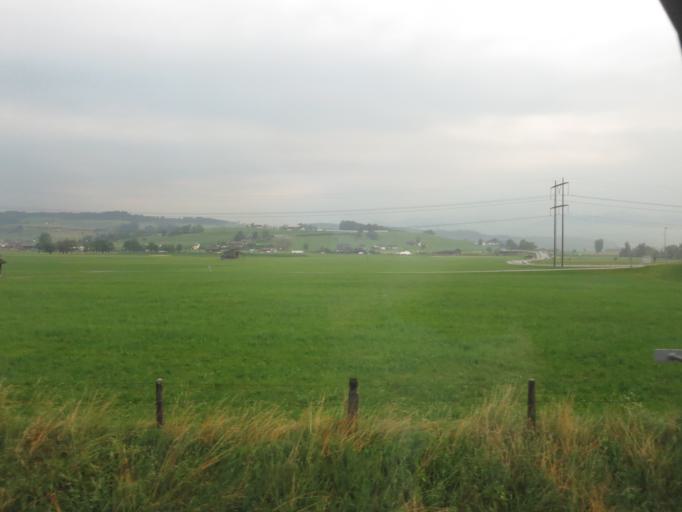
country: CH
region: Schwyz
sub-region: Bezirk March
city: Schubelbach
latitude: 47.1768
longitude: 8.9408
